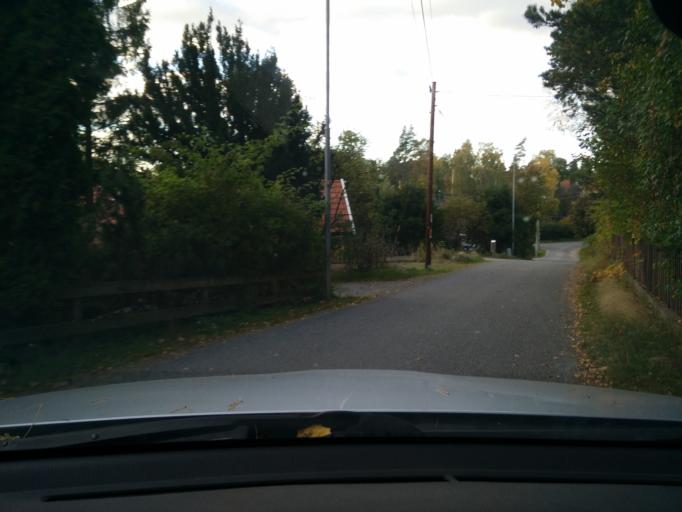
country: SE
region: Stockholm
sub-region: Stockholms Kommun
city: Kista
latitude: 59.4119
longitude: 17.9521
